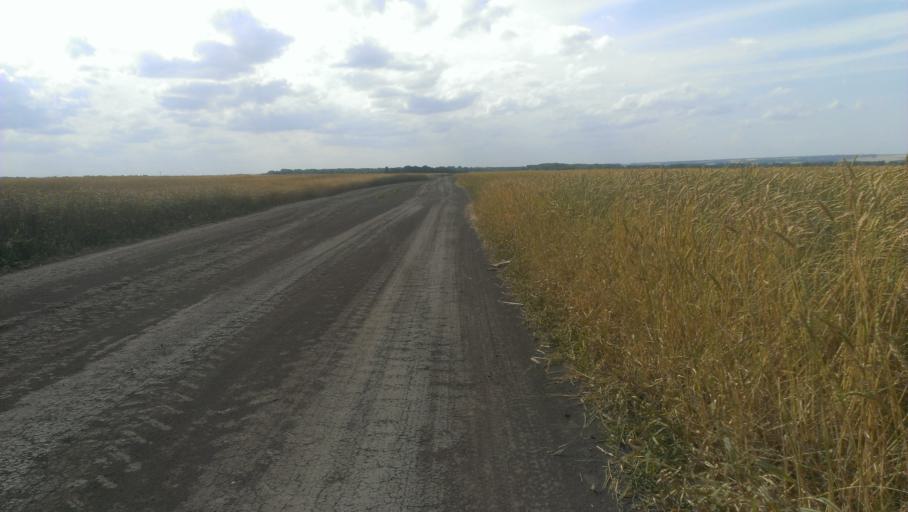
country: RU
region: Altai Krai
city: Gon'ba
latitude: 53.3743
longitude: 83.5511
